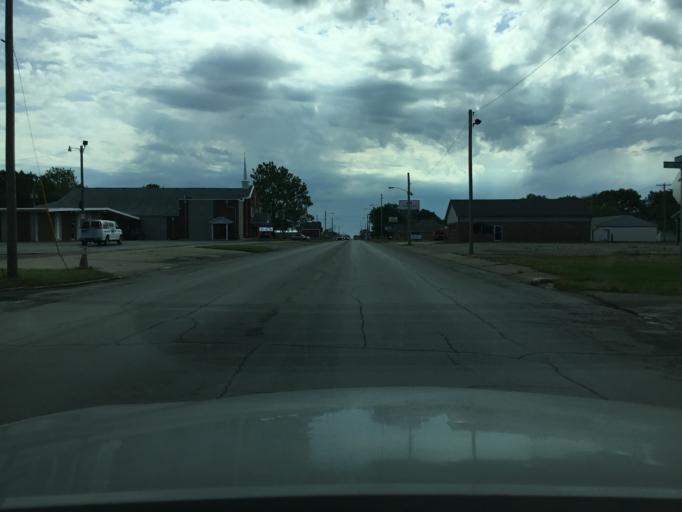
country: US
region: Kansas
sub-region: Montgomery County
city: Coffeyville
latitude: 37.0363
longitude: -95.6416
